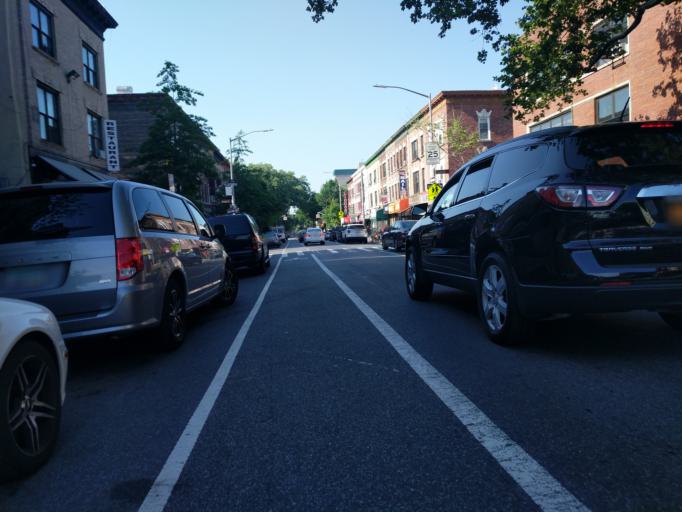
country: US
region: New York
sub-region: Kings County
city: Brooklyn
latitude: 40.6700
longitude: -73.9422
